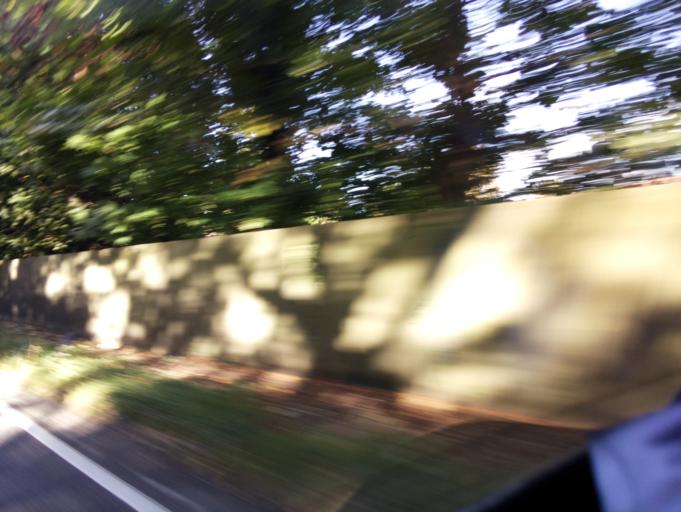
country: GB
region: England
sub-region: Hampshire
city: Swanmore
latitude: 50.9538
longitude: -1.1394
